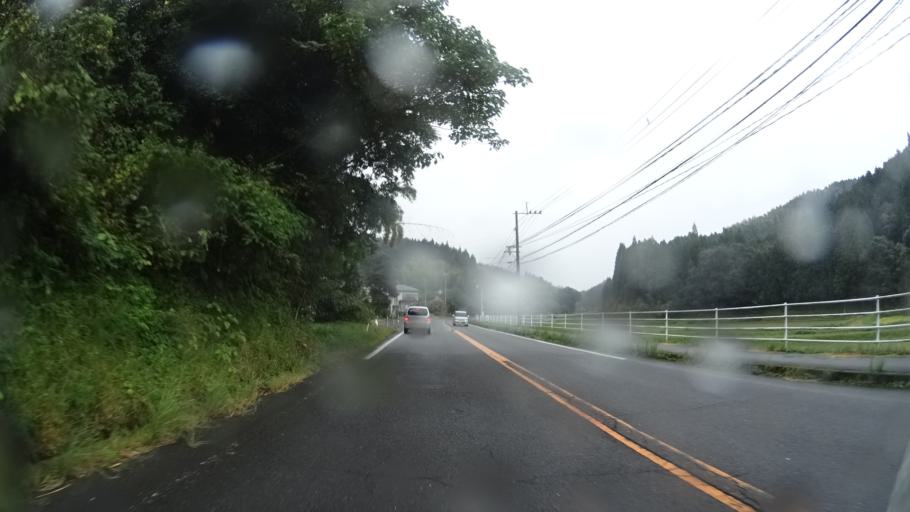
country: JP
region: Kagoshima
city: Kajiki
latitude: 31.8210
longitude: 130.6775
